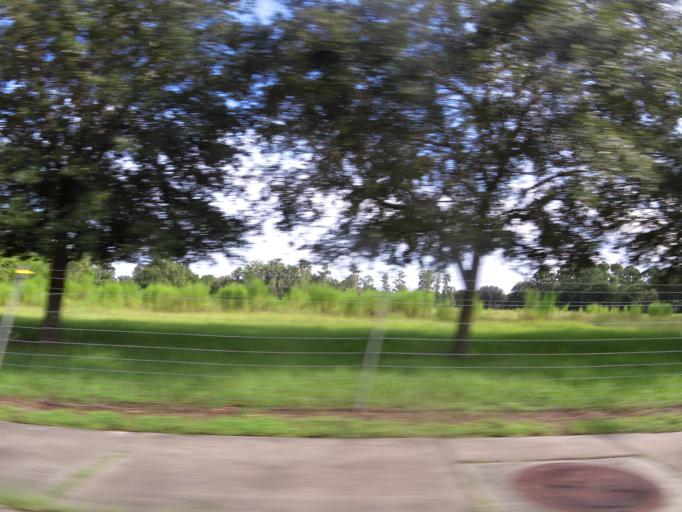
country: US
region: Florida
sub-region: Saint Johns County
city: Fruit Cove
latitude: 30.1861
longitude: -81.5968
